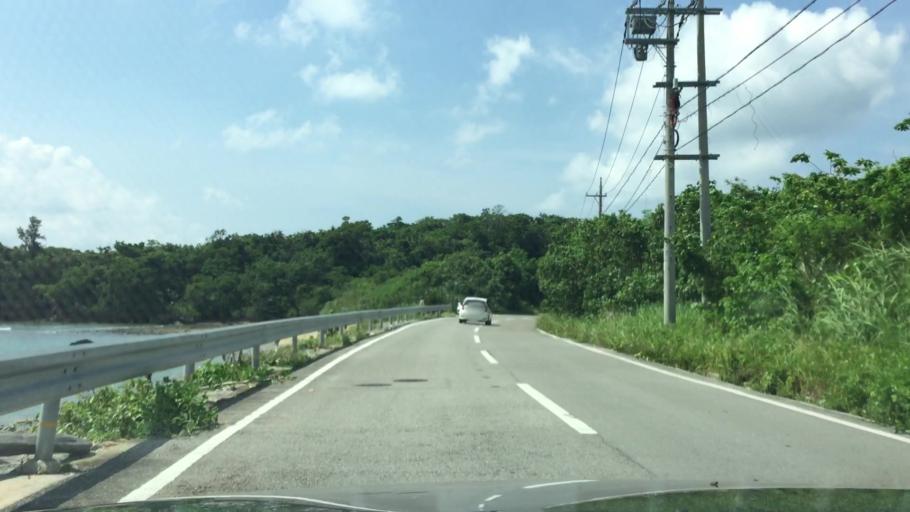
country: JP
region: Okinawa
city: Ishigaki
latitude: 24.4666
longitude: 124.2259
